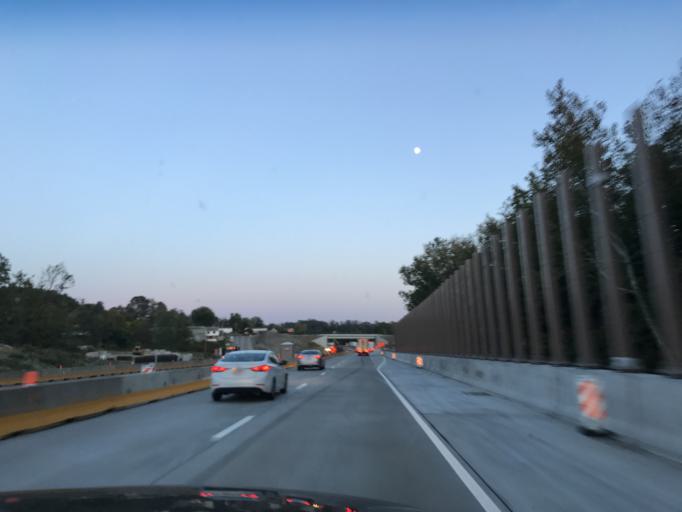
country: US
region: Pennsylvania
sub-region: Washington County
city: Bentleyville
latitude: 40.1356
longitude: -80.0102
